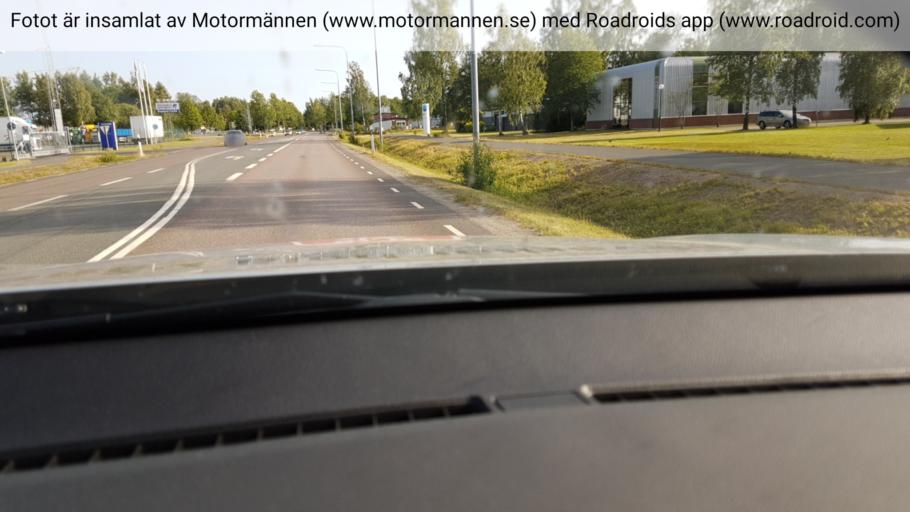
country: SE
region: Joenkoeping
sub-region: Varnamo Kommun
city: Varnamo
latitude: 57.1912
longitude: 14.0634
